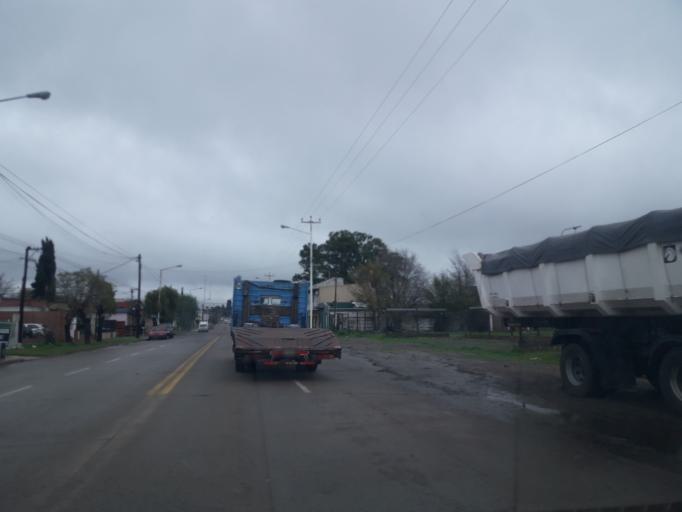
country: AR
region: Buenos Aires
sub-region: Partido de Tandil
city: Tandil
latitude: -37.3176
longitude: -59.1558
